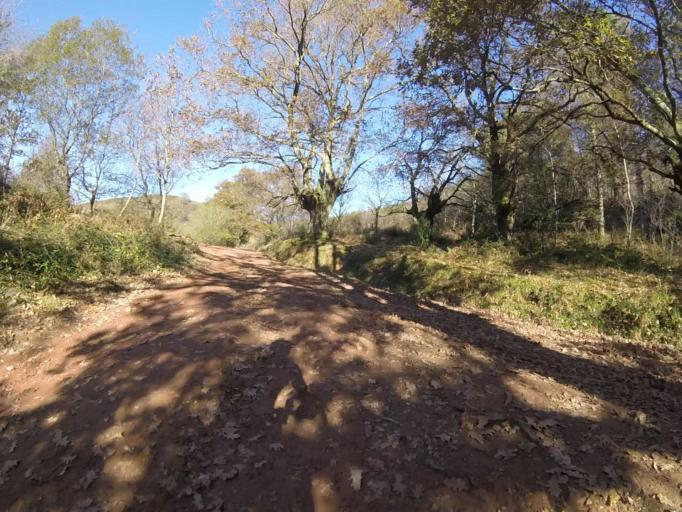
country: ES
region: Navarre
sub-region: Provincia de Navarra
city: Bera
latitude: 43.3191
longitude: -1.6997
